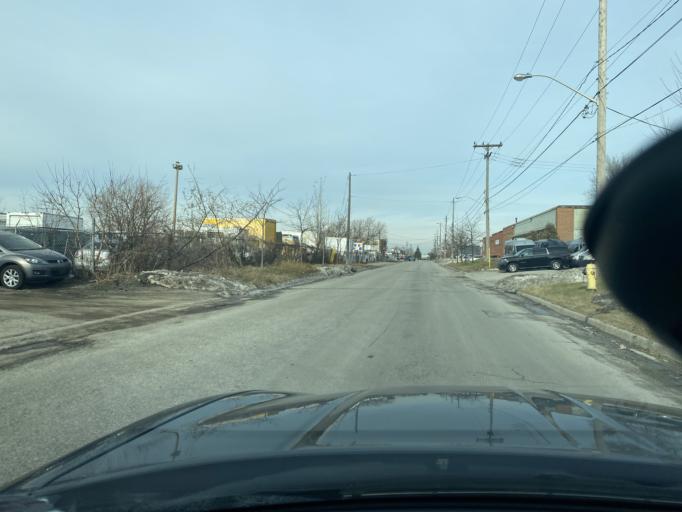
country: CA
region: Ontario
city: Scarborough
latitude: 43.7227
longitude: -79.2819
